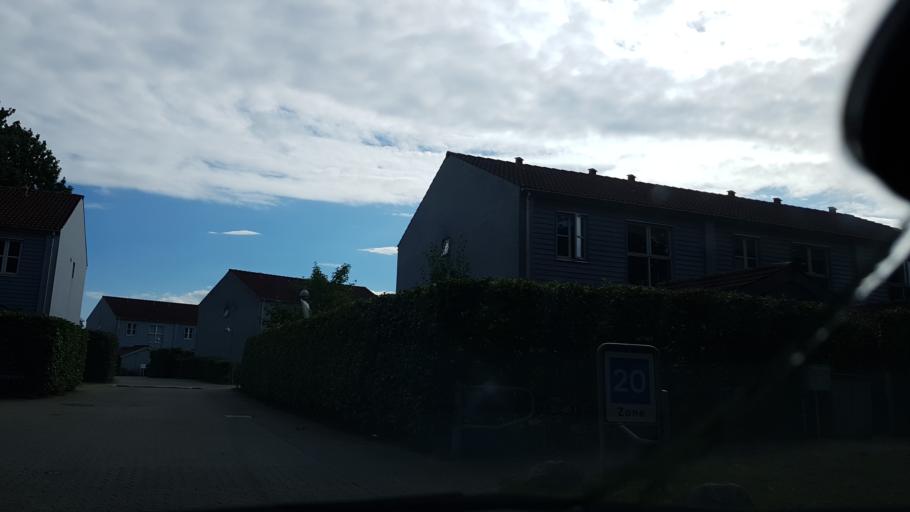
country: DK
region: Capital Region
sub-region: Fredensborg Kommune
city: Humlebaek
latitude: 55.9859
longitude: 12.5272
